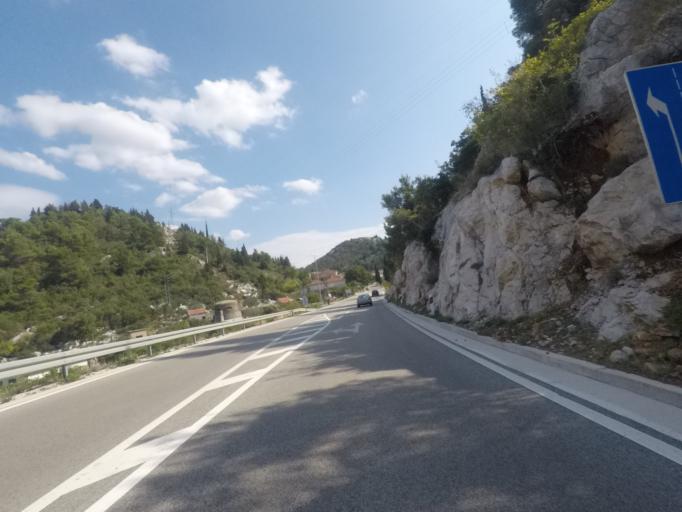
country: HR
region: Dubrovacko-Neretvanska
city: Komin
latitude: 43.0694
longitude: 17.4230
